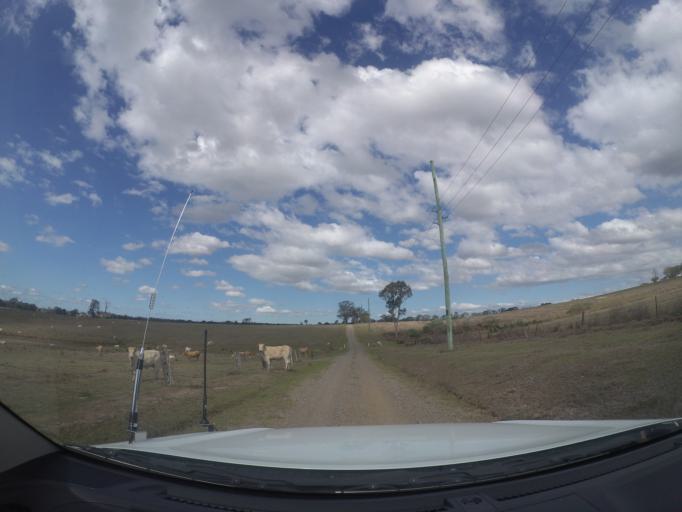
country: AU
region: Queensland
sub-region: Logan
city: North Maclean
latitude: -27.8080
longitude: 152.9993
